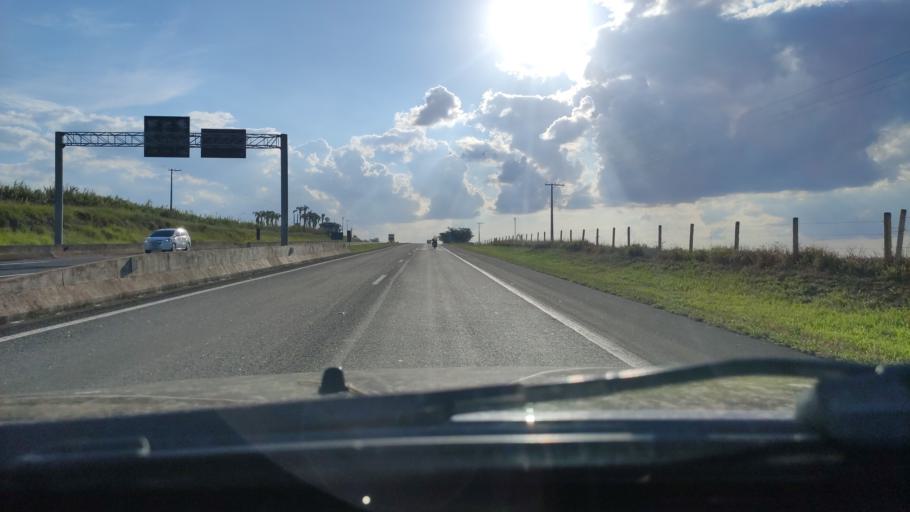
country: BR
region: Sao Paulo
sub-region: Mogi-Mirim
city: Mogi Mirim
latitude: -22.4563
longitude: -46.9111
